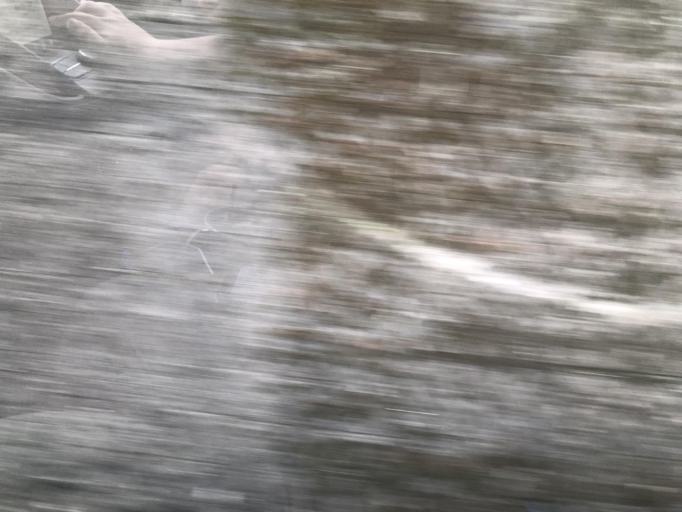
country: TW
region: Taiwan
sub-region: Taoyuan
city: Taoyuan
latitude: 24.9255
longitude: 121.3803
